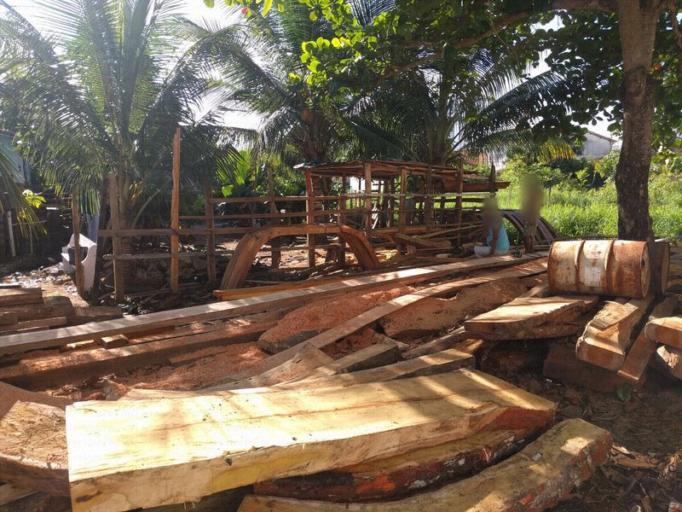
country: BR
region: Bahia
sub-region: Valenca
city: Valenca
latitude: -13.3701
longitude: -39.0680
